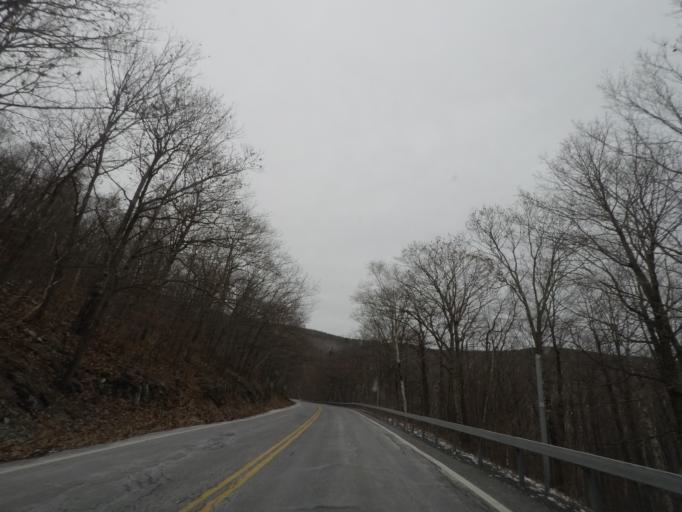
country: US
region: Massachusetts
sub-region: Berkshire County
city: Williamstown
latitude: 42.7361
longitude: -73.2801
